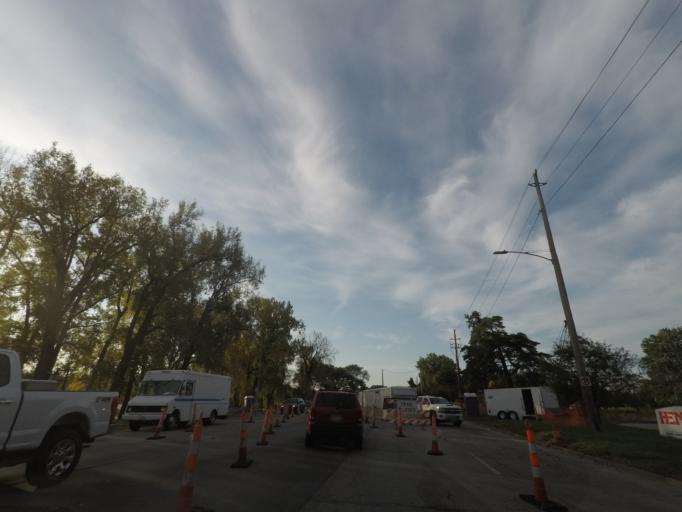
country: US
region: Iowa
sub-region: Polk County
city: Des Moines
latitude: 41.5707
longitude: -93.6450
